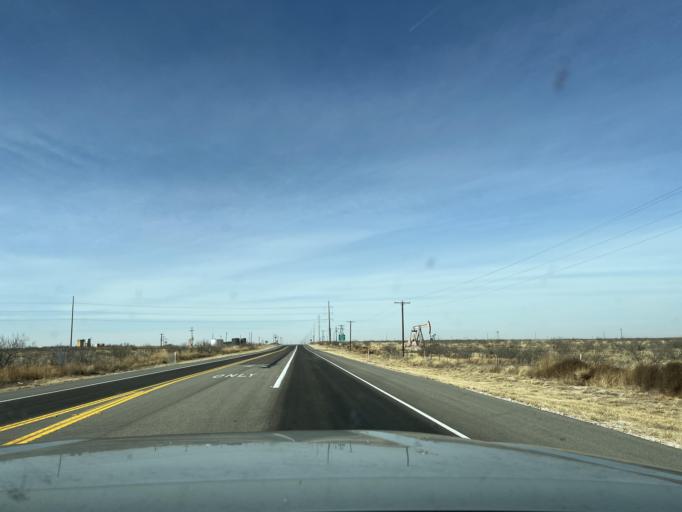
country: US
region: Texas
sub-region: Andrews County
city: Andrews
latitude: 32.3331
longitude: -102.6541
